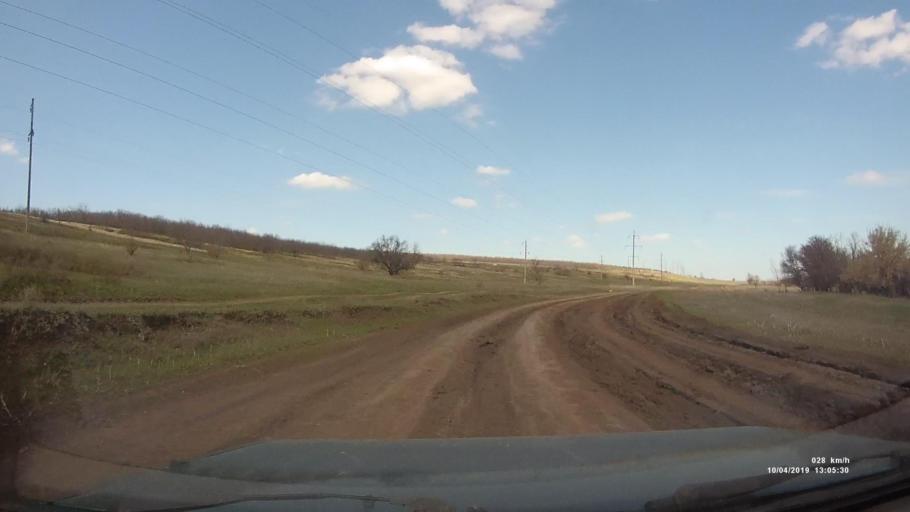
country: RU
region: Rostov
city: Masalovka
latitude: 48.3882
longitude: 40.2328
